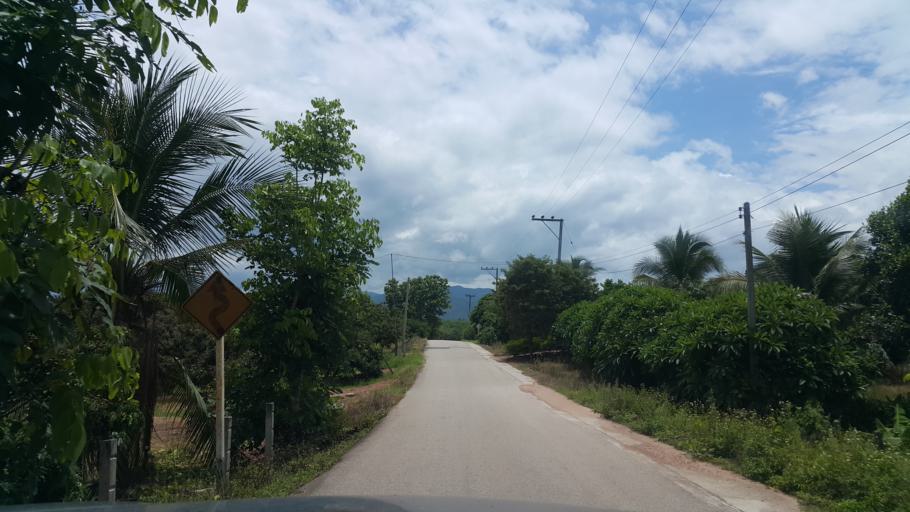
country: TH
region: Chiang Mai
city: Mae Taeng
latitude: 19.2043
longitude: 99.0072
